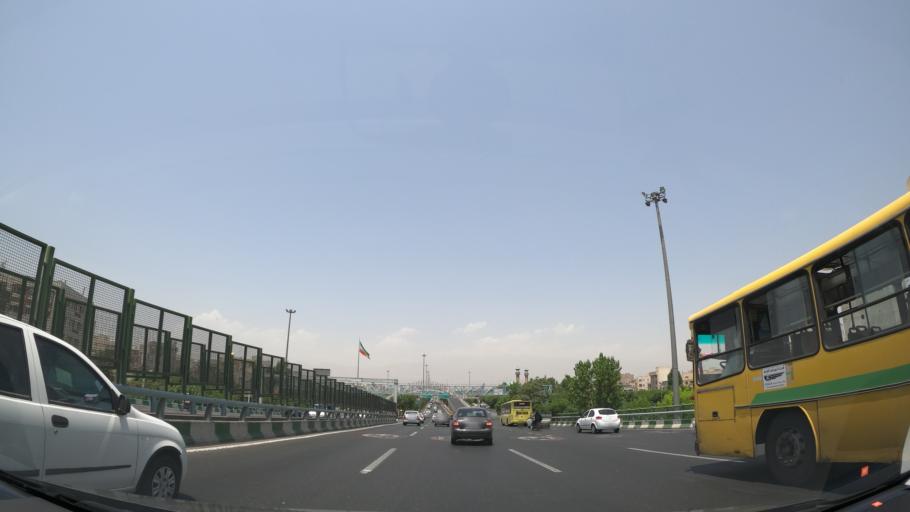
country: IR
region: Tehran
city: Tehran
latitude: 35.6607
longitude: 51.3822
